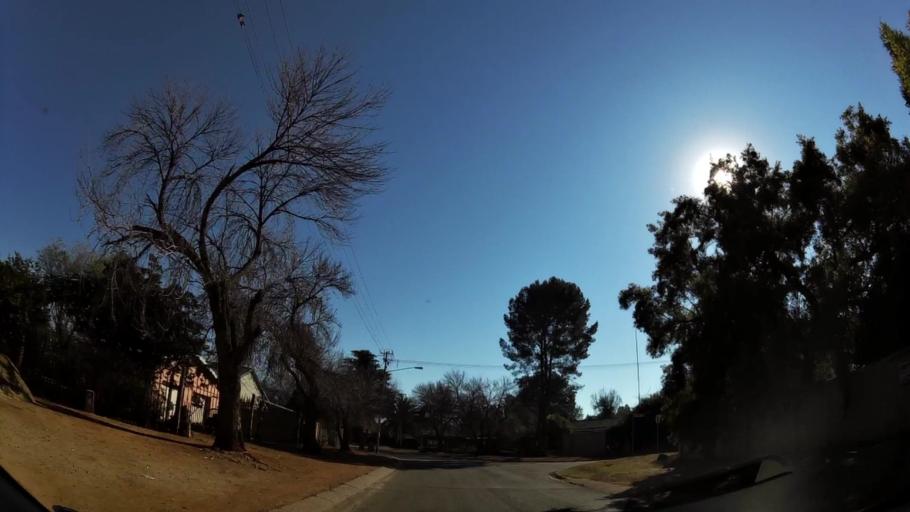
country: ZA
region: Gauteng
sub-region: City of Tshwane Metropolitan Municipality
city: Centurion
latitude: -25.8539
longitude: 28.2094
